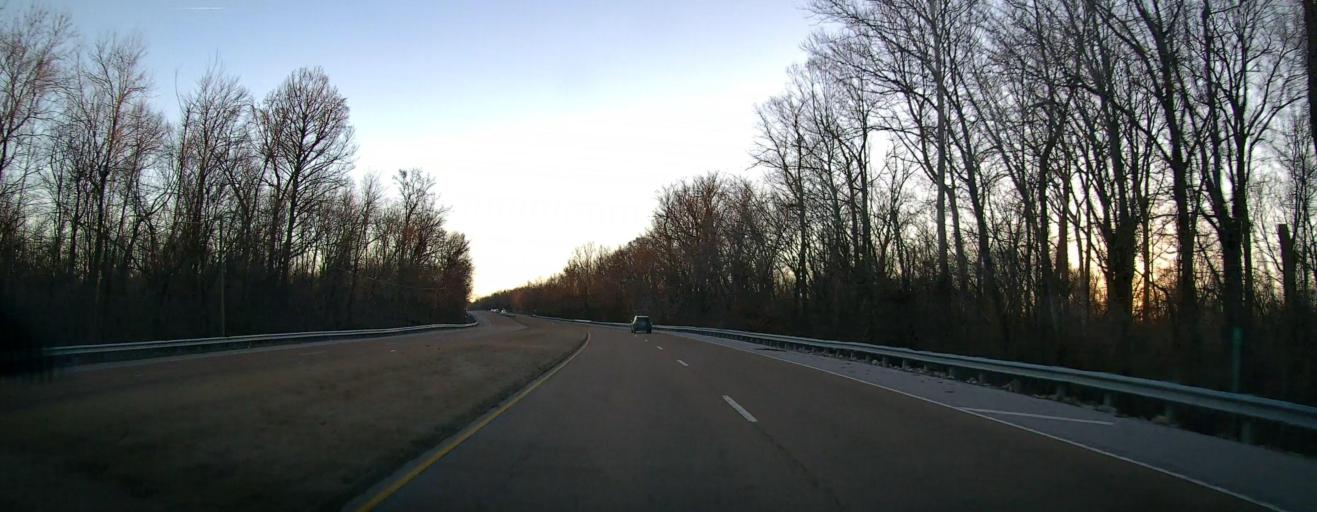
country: US
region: Tennessee
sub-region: Shelby County
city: Millington
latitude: 35.2796
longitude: -89.8865
